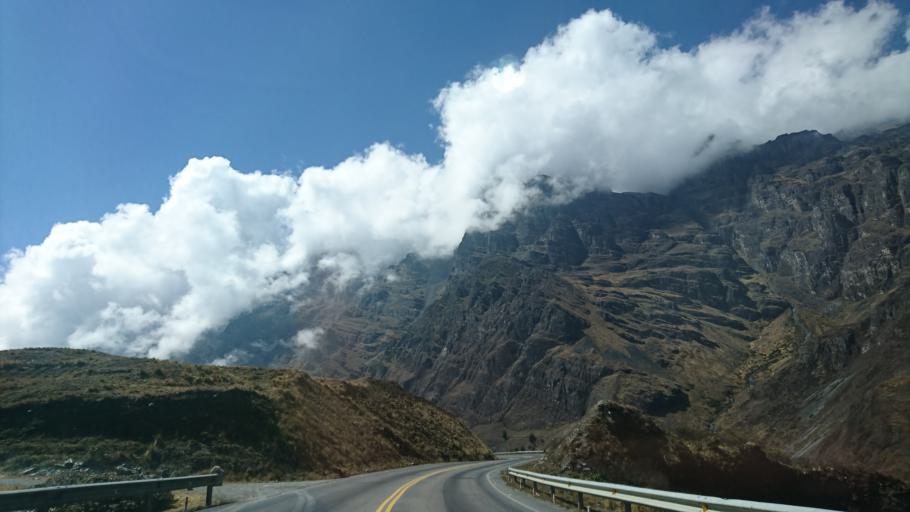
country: BO
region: La Paz
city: La Paz
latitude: -16.3291
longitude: -67.9666
